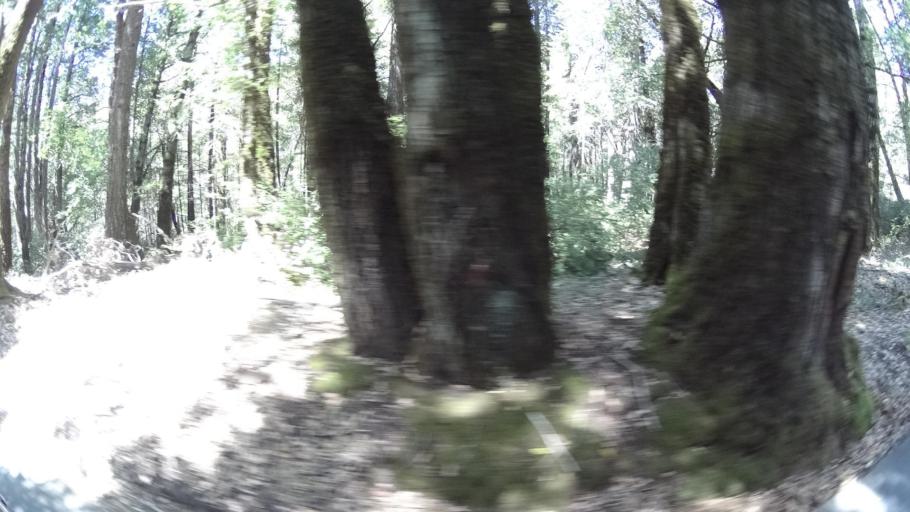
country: US
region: California
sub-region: Humboldt County
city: Redway
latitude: 40.0886
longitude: -123.9477
